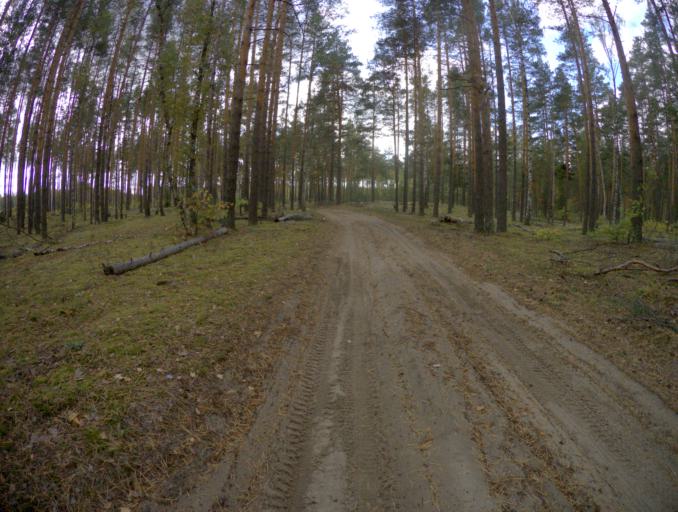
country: RU
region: Moskovskaya
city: Baksheyevo
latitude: 55.7252
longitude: 39.8453
